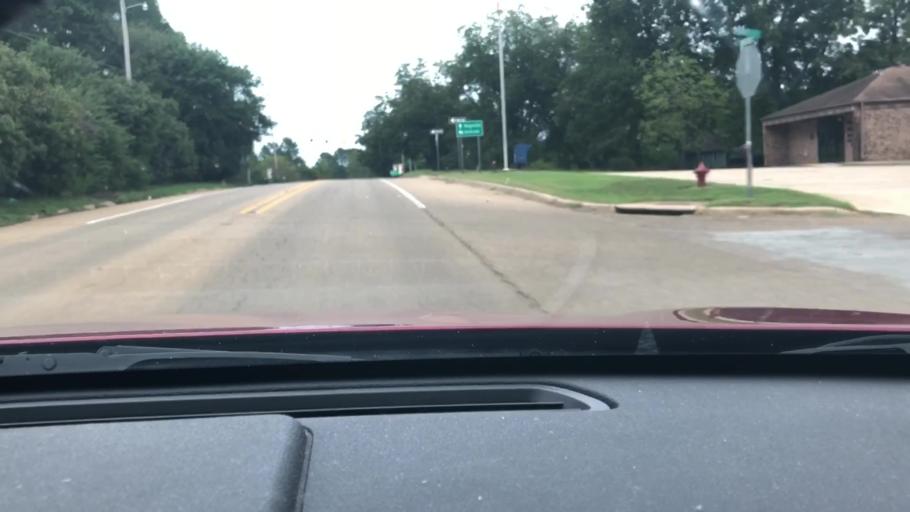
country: US
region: Arkansas
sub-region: Lafayette County
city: Stamps
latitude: 33.3585
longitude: -93.4361
